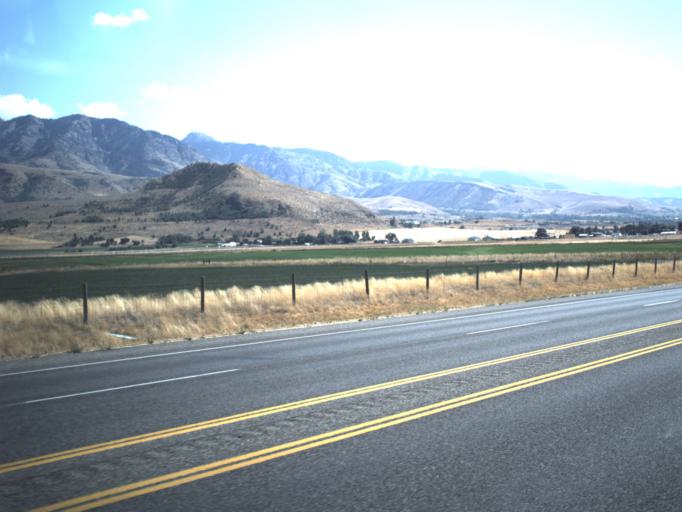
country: US
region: Utah
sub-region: Cache County
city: Lewiston
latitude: 41.9806
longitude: -111.8129
